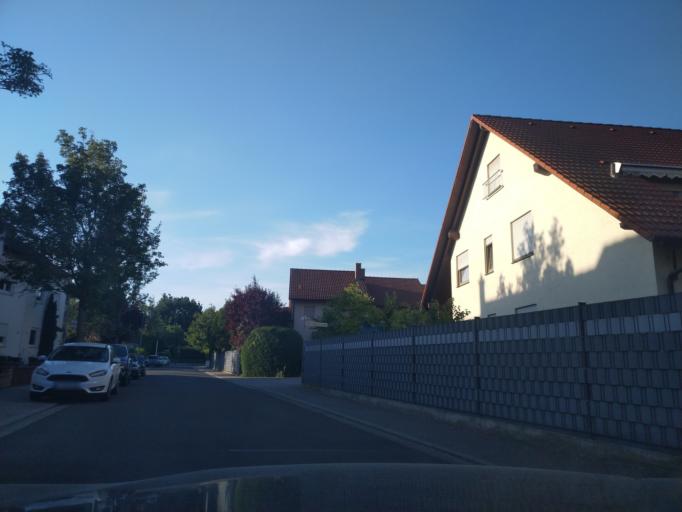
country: DE
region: Rheinland-Pfalz
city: Frankenthal
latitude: 49.5186
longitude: 8.3606
